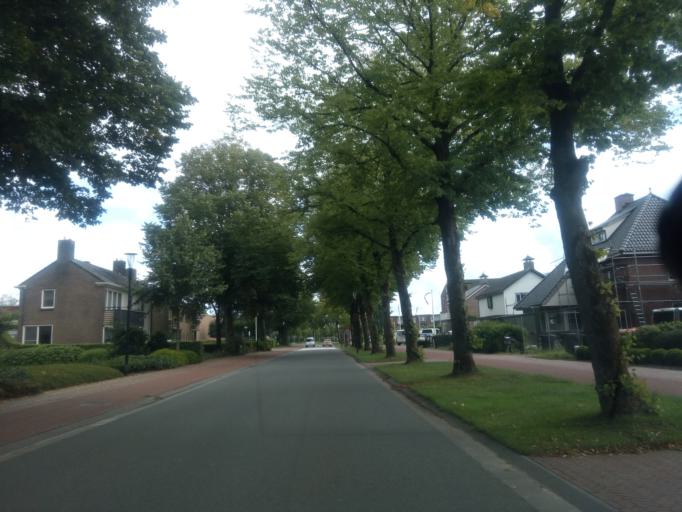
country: NL
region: Friesland
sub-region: Gemeente Achtkarspelen
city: Surhuisterveen
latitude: 53.1806
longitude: 6.1638
